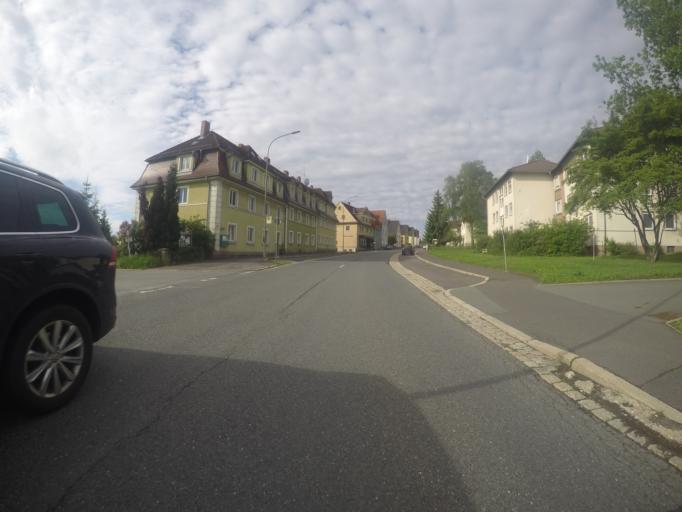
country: DE
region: Bavaria
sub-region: Upper Franconia
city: Schonwald
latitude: 50.2019
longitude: 12.0946
